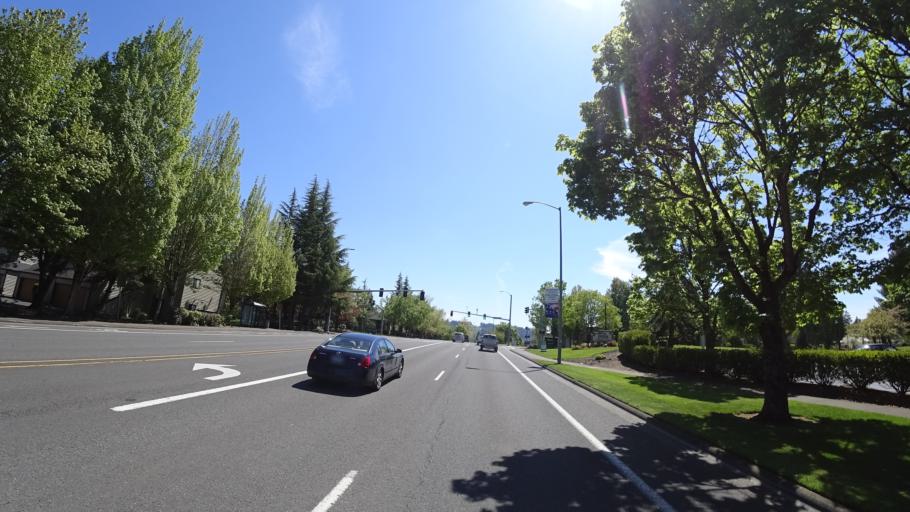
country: US
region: Oregon
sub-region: Washington County
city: King City
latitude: 45.4435
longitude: -122.8261
